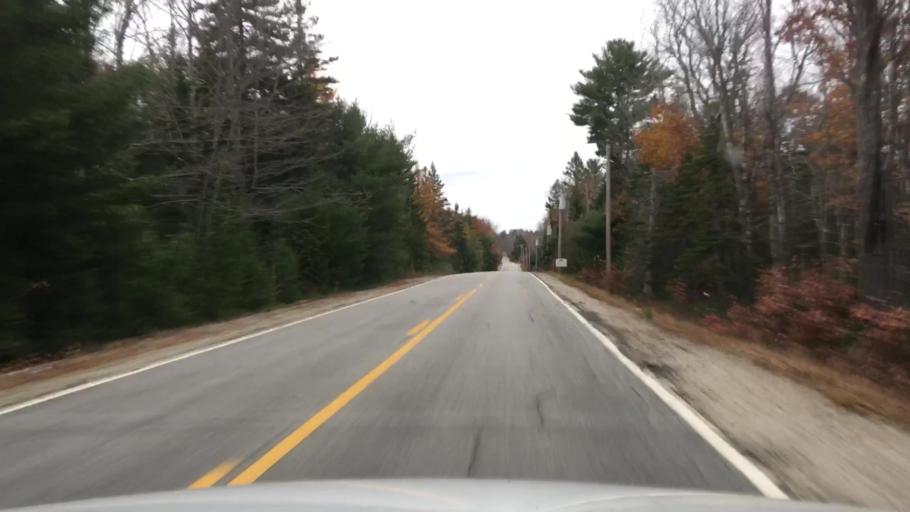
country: US
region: Maine
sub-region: Hancock County
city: Sedgwick
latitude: 44.3118
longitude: -68.5706
